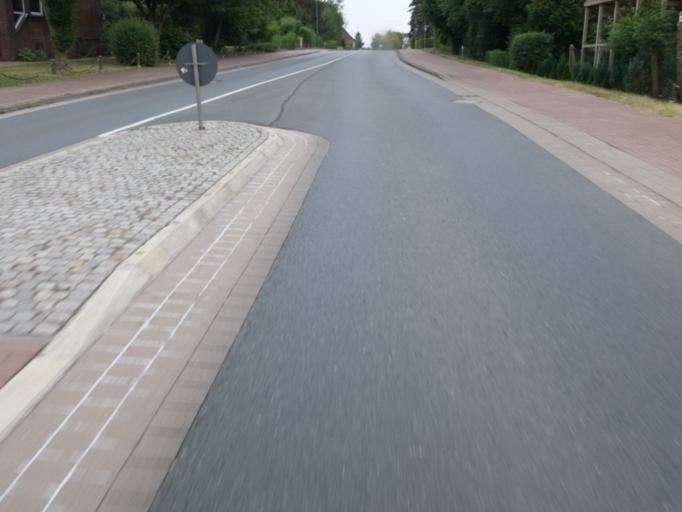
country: DE
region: Lower Saxony
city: Leese
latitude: 52.4641
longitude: 9.1446
